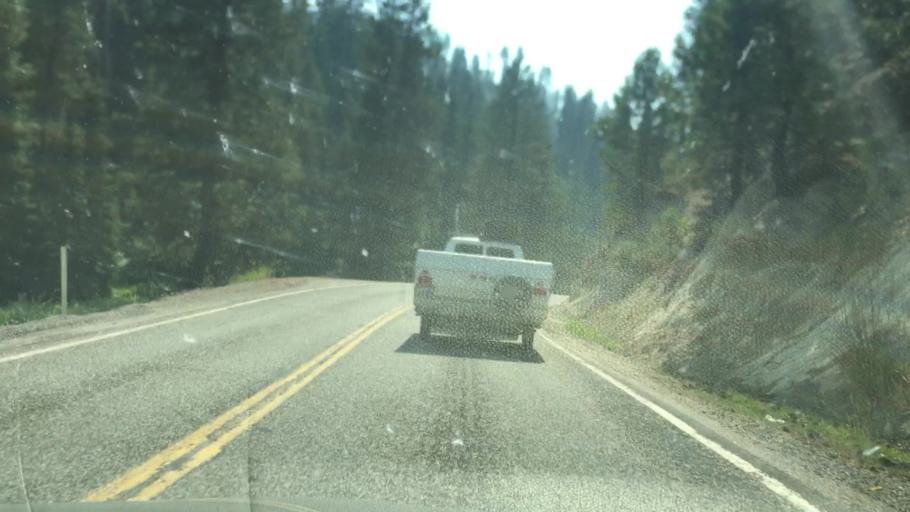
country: US
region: Idaho
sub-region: Valley County
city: Cascade
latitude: 44.3349
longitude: -116.0481
